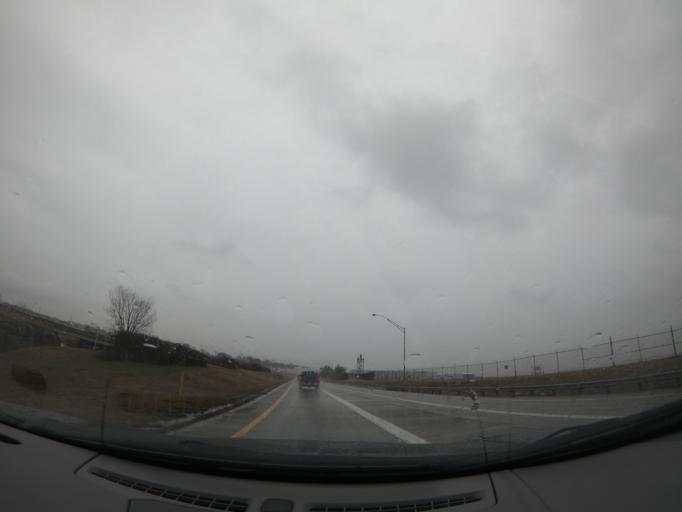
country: US
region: Kentucky
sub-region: Jefferson County
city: Audubon Park
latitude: 38.1886
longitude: -85.7293
